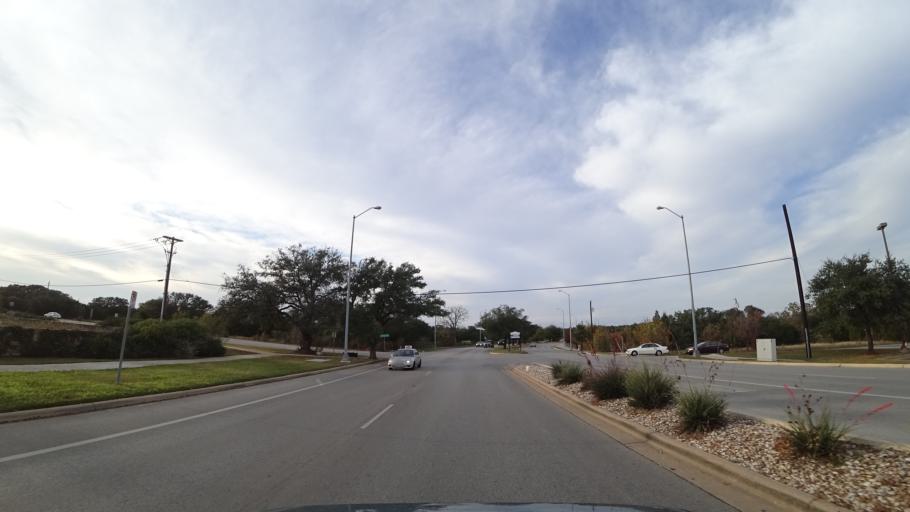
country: US
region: Texas
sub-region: Williamson County
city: Brushy Creek
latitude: 30.5081
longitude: -97.7165
